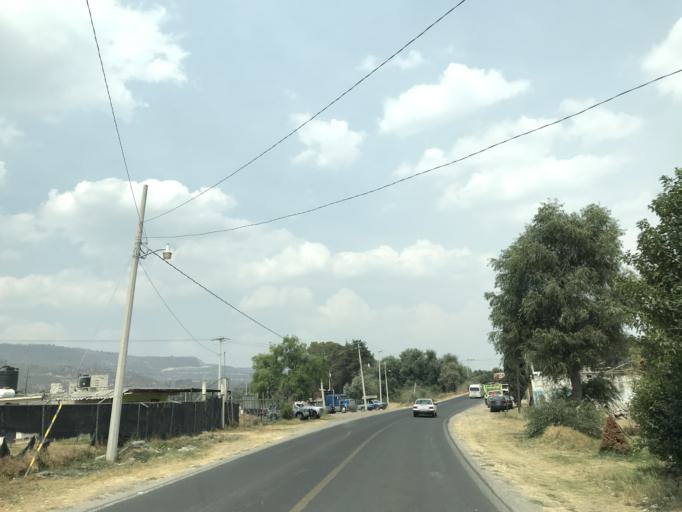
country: MX
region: Tlaxcala
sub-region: Panotla
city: Fraccionamiento la Virgen
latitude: 19.3200
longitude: -98.3066
